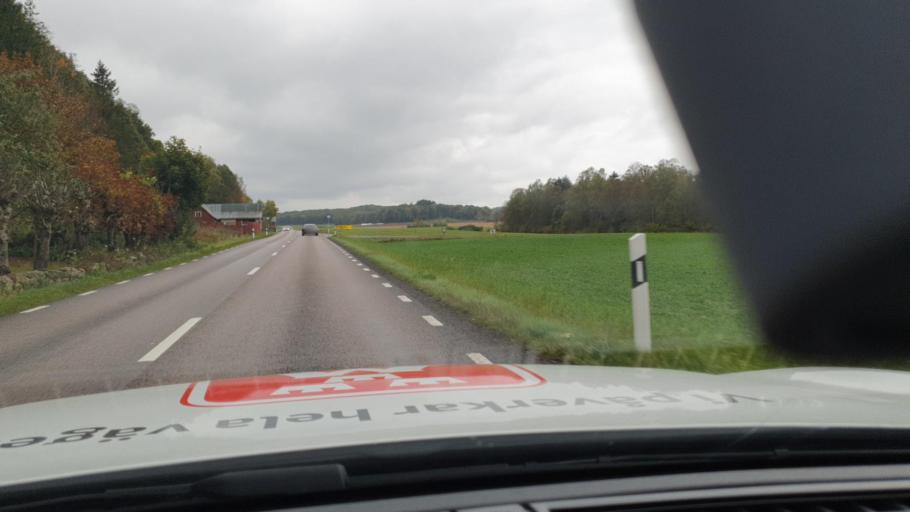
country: SE
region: Halland
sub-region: Falkenbergs Kommun
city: Falkenberg
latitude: 57.0499
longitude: 12.6108
